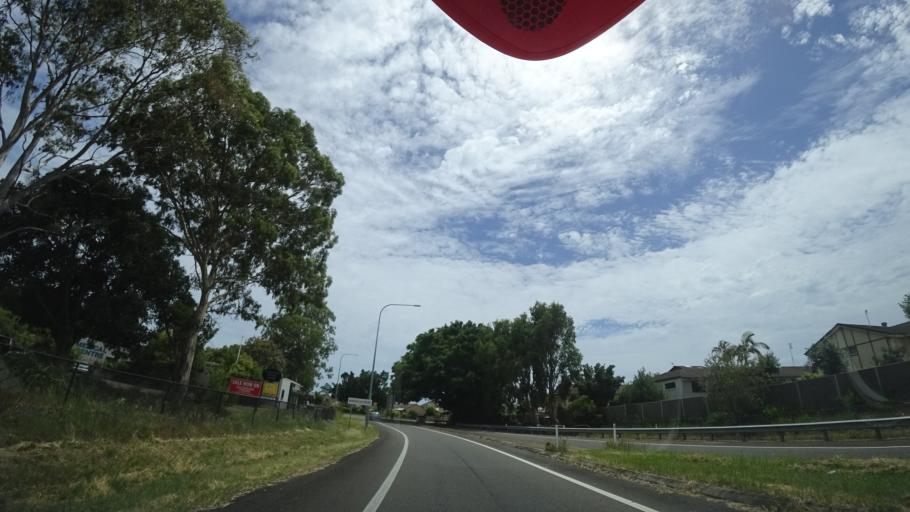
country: AU
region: Queensland
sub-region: Sunshine Coast
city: Buderim
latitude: -26.6455
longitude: 153.0681
